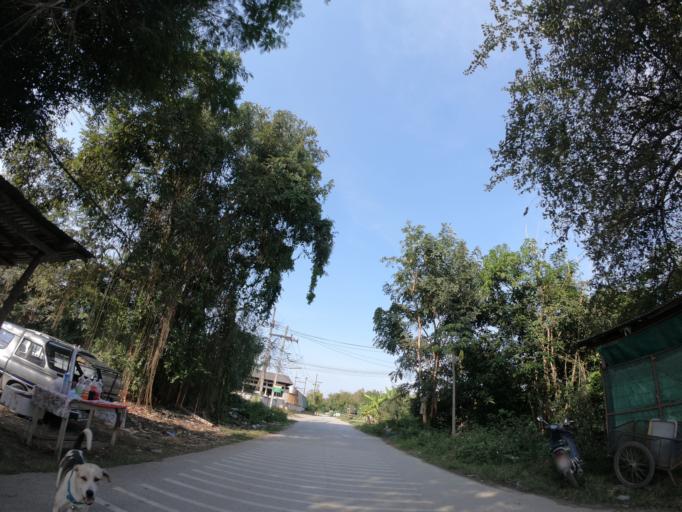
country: TH
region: Chiang Mai
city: Chiang Mai
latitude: 18.8306
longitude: 98.9905
